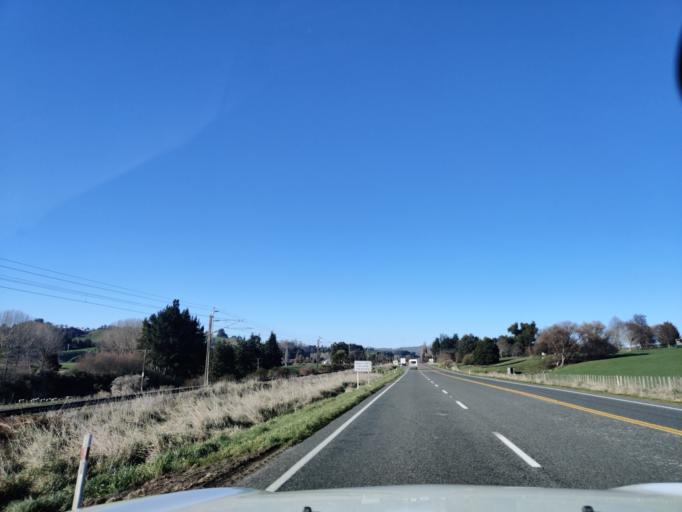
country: NZ
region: Manawatu-Wanganui
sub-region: Ruapehu District
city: Waiouru
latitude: -39.7215
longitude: 175.8411
